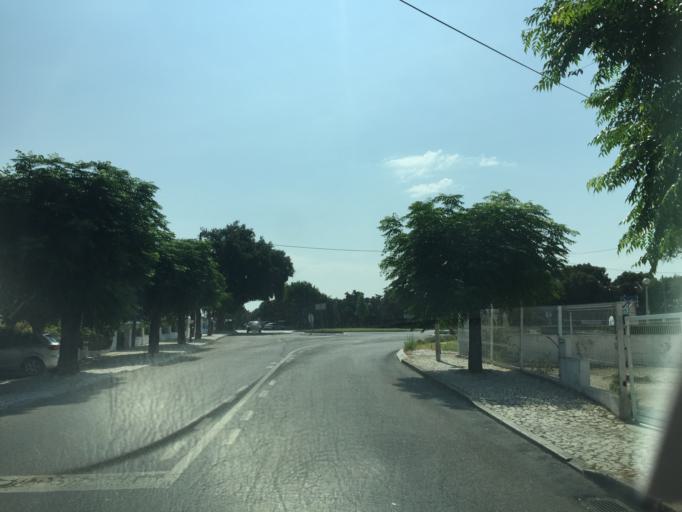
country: PT
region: Setubal
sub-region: Setubal
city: Setubal
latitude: 38.5831
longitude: -8.6891
